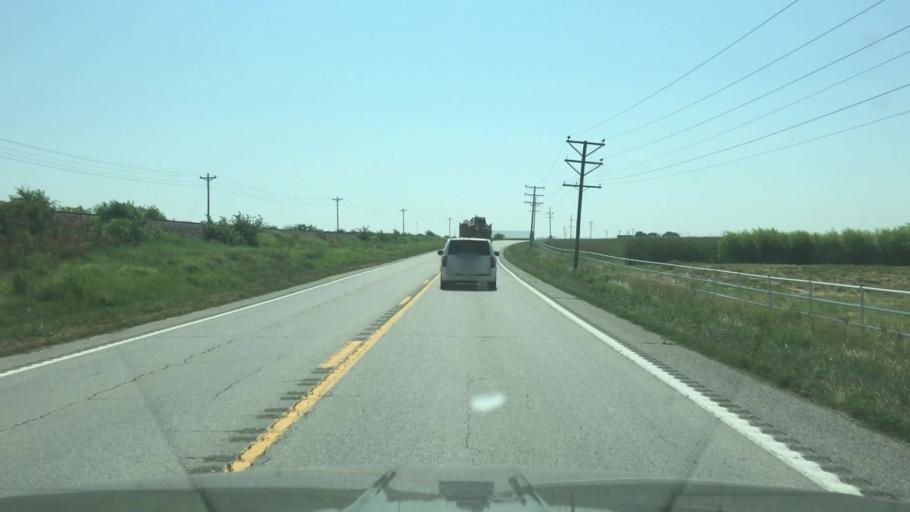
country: US
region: Missouri
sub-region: Moniteau County
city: Tipton
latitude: 38.6704
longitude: -92.8481
